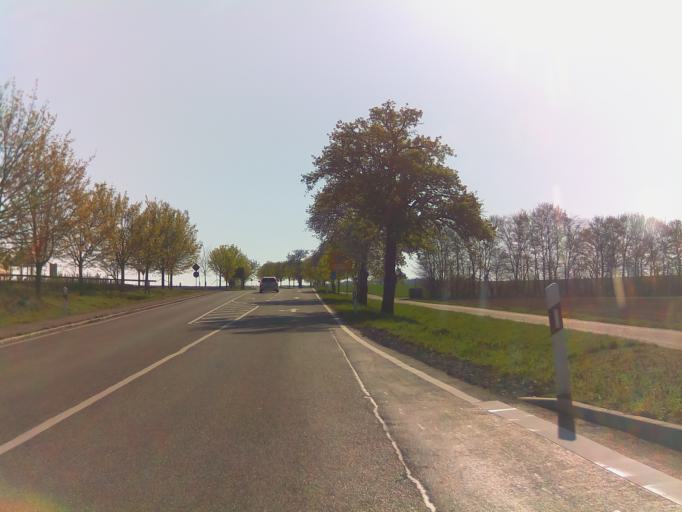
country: DE
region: Baden-Wuerttemberg
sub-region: Regierungsbezirk Stuttgart
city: Wolpertshausen
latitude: 49.1686
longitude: 9.8583
